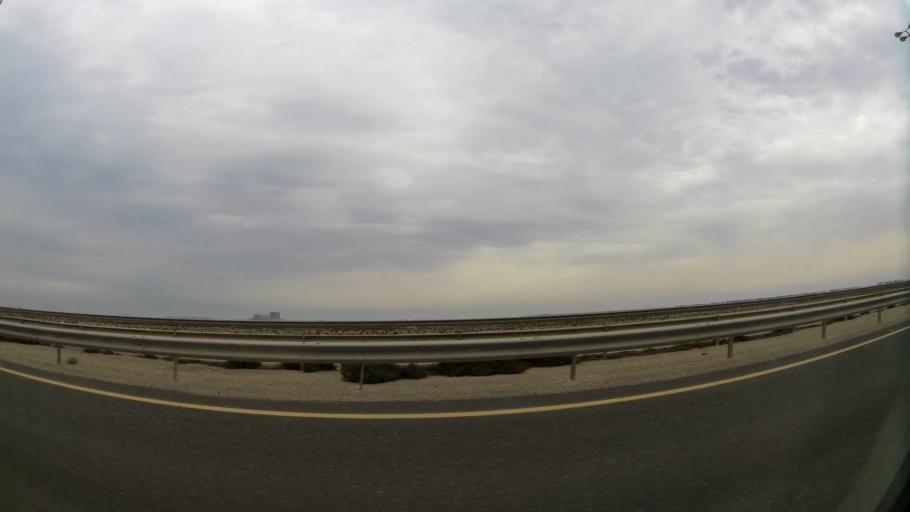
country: BH
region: Central Governorate
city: Dar Kulayb
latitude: 25.8596
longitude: 50.5850
